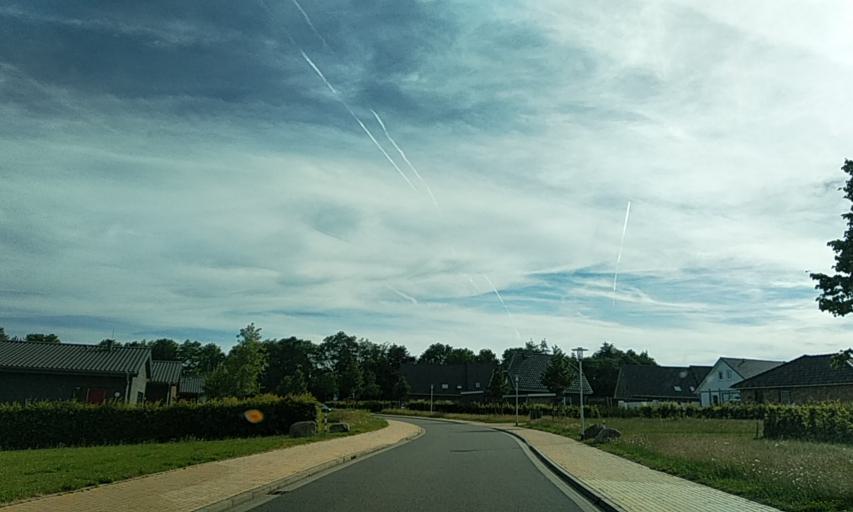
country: DE
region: Schleswig-Holstein
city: Schleswig
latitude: 54.5353
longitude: 9.5629
